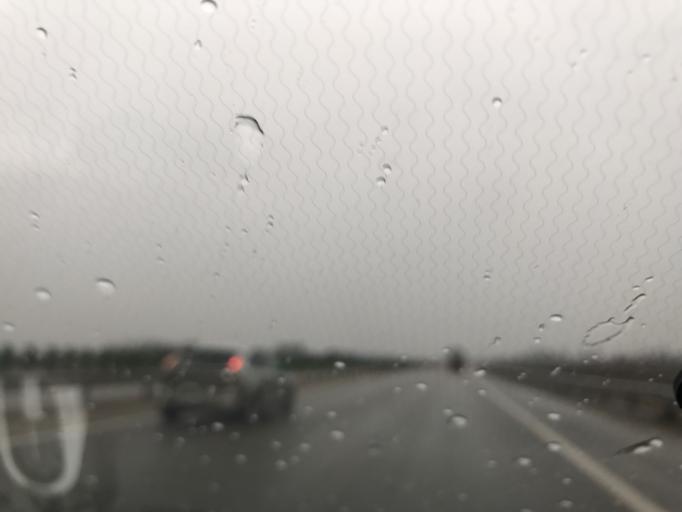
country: RU
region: Krasnodarskiy
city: Krylovskaya
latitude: 46.2914
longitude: 39.8228
